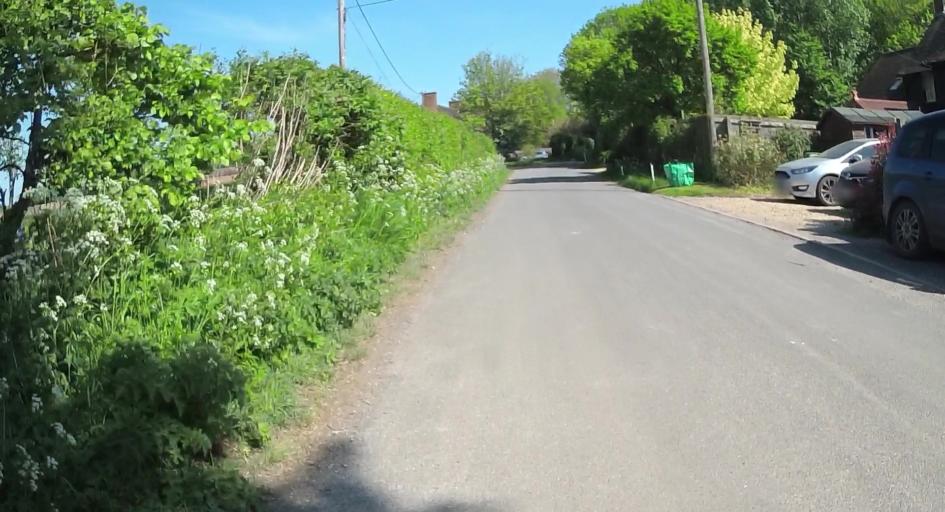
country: GB
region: England
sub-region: Hampshire
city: Kings Worthy
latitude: 51.1510
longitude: -1.2885
